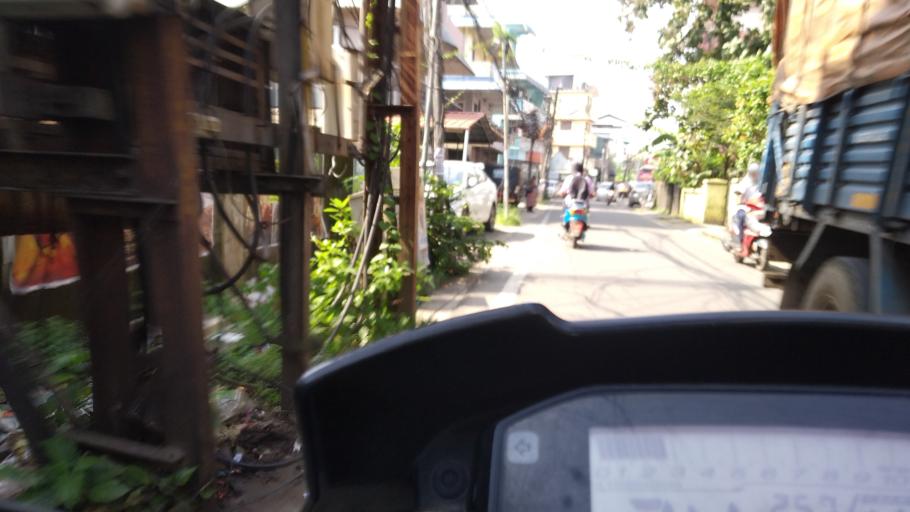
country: IN
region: Kerala
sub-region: Ernakulam
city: Cochin
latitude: 9.9803
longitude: 76.2869
